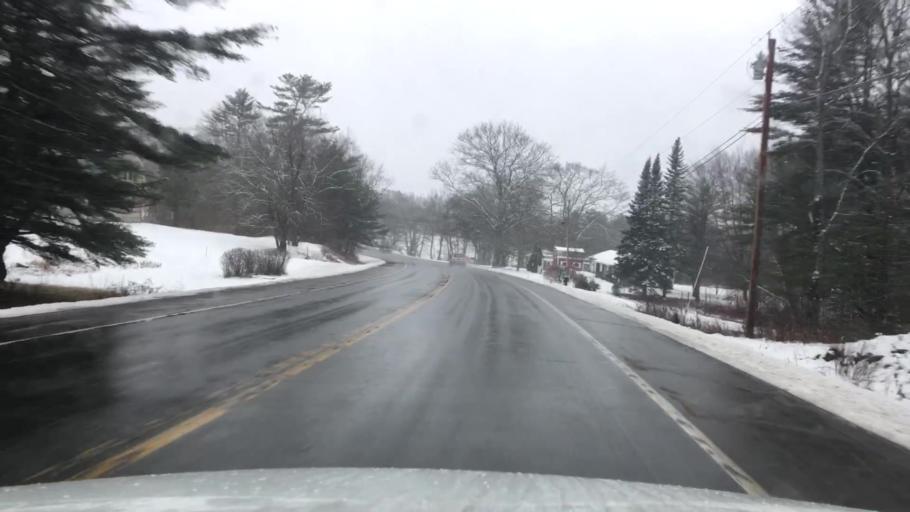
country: US
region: Maine
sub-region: Knox County
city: Warren
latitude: 44.1362
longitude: -69.2230
